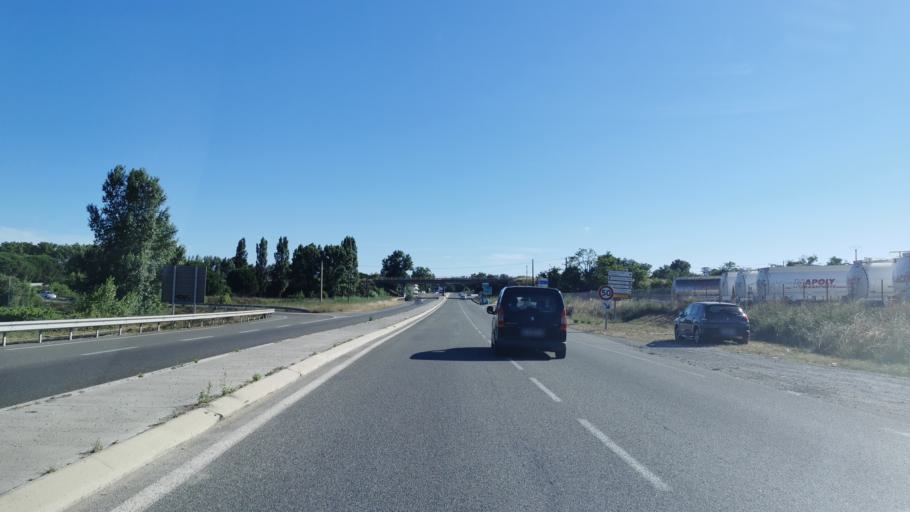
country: FR
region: Languedoc-Roussillon
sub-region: Departement de l'Herault
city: Beziers
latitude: 43.3242
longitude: 3.1899
